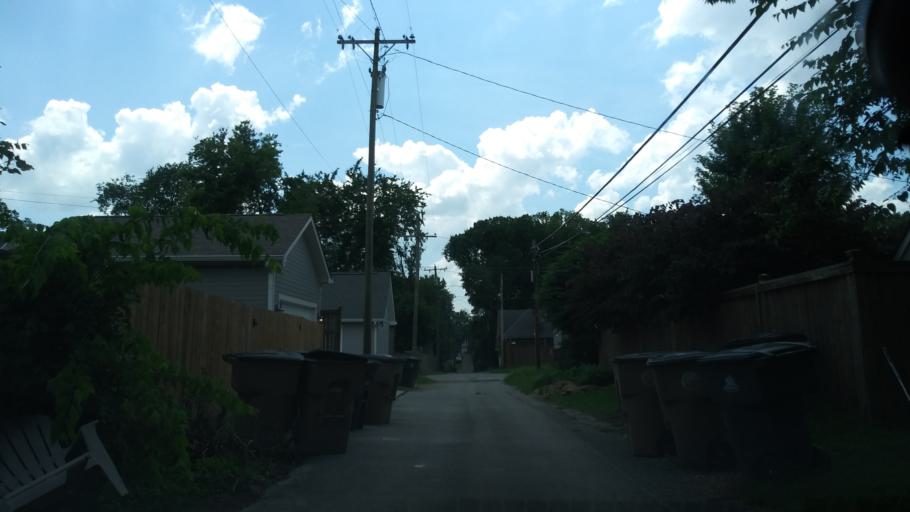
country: US
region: Tennessee
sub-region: Davidson County
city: Belle Meade
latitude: 36.1505
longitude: -86.8416
